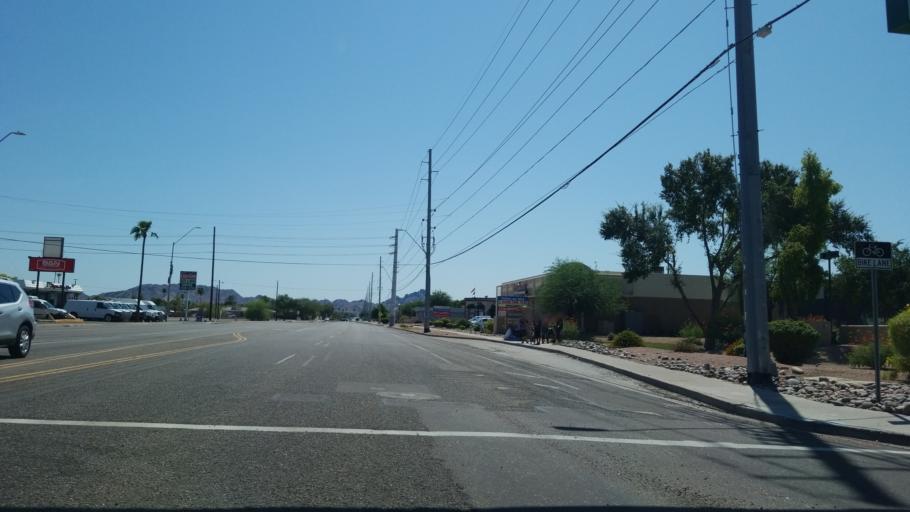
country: US
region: Arizona
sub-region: Maricopa County
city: Paradise Valley
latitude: 33.6267
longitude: -112.0147
